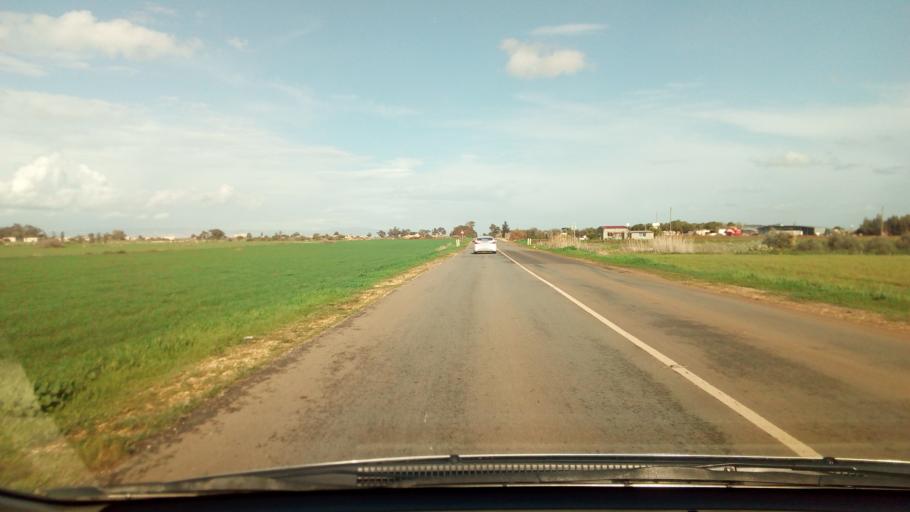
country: CY
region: Ammochostos
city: Achna
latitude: 35.0496
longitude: 33.7921
